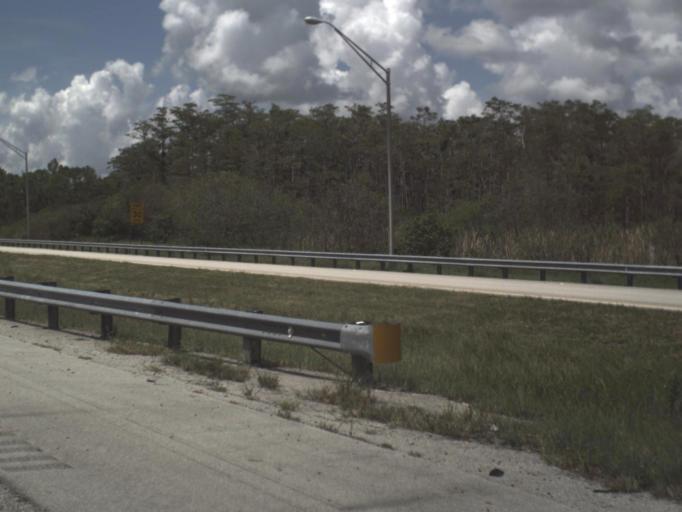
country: US
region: Florida
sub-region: Collier County
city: Immokalee
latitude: 26.1687
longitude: -81.0684
